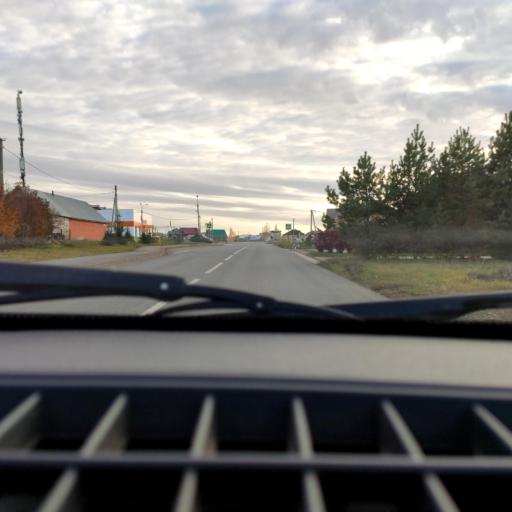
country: RU
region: Bashkortostan
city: Avdon
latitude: 54.6994
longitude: 55.7971
